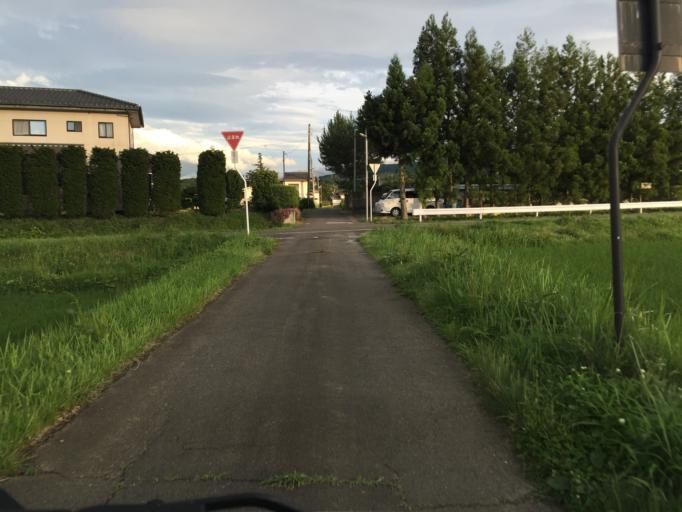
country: JP
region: Fukushima
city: Fukushima-shi
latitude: 37.7185
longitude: 140.3835
